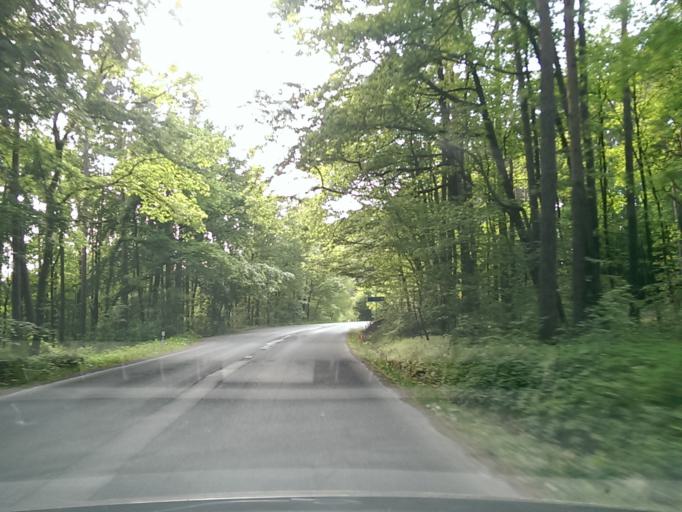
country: CZ
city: Duba
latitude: 50.5546
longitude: 14.5897
